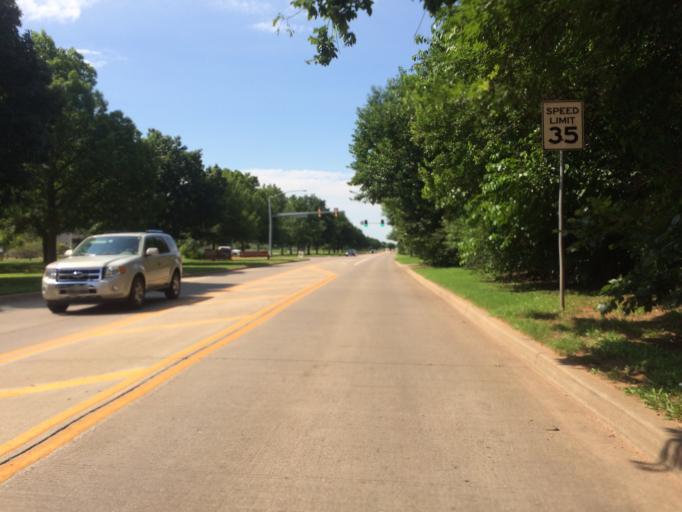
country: US
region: Oklahoma
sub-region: Cleveland County
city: Norman
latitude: 35.1960
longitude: -97.4501
